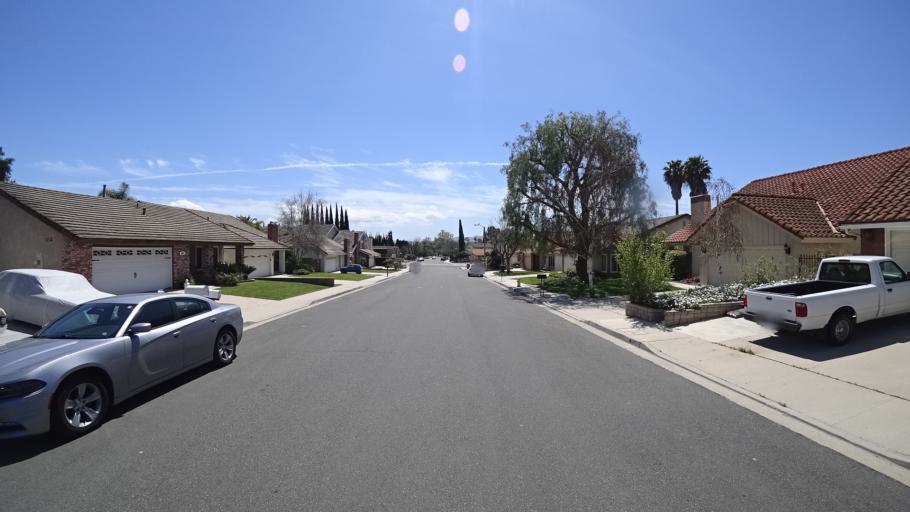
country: US
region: California
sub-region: Ventura County
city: Thousand Oaks
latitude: 34.2169
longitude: -118.8479
